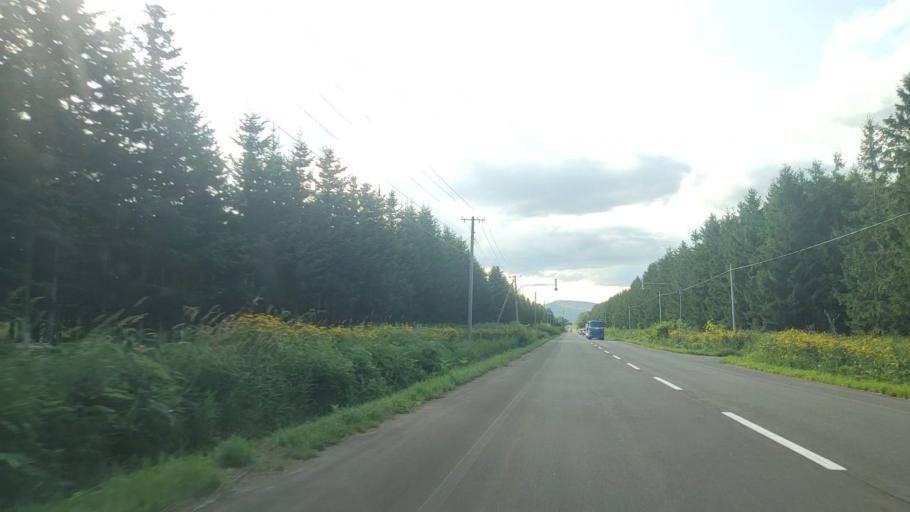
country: JP
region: Hokkaido
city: Makubetsu
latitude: 44.8876
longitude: 142.0068
